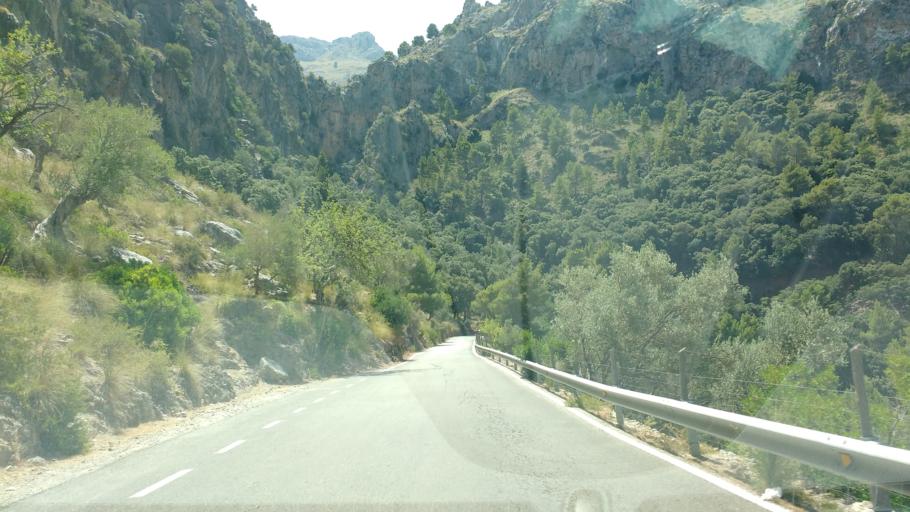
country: ES
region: Balearic Islands
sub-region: Illes Balears
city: Escorca
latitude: 39.8402
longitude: 2.7990
